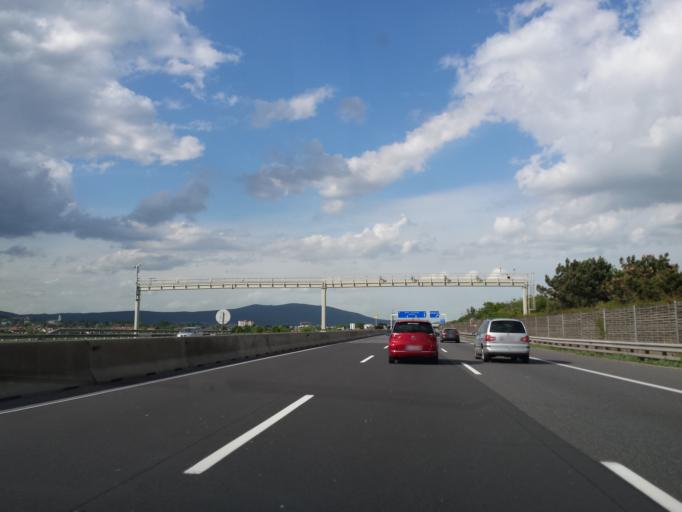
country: AT
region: Lower Austria
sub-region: Politischer Bezirk Baden
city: Kottingbrunn
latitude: 47.9473
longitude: 16.2157
